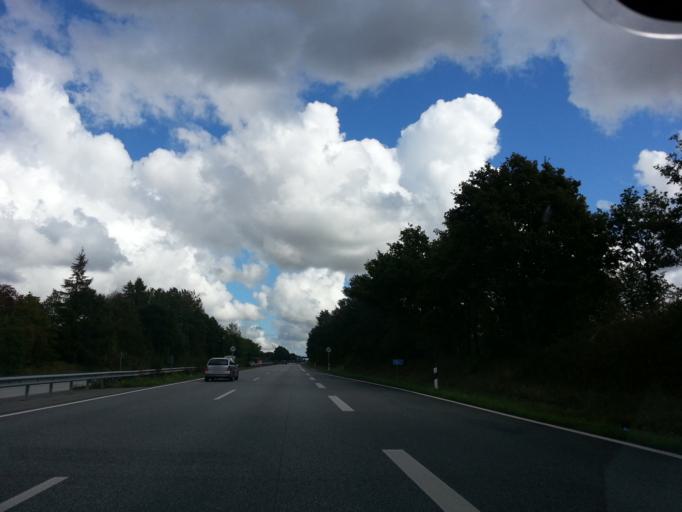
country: DE
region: Schleswig-Holstein
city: Beschendorf
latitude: 54.1567
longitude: 10.8583
